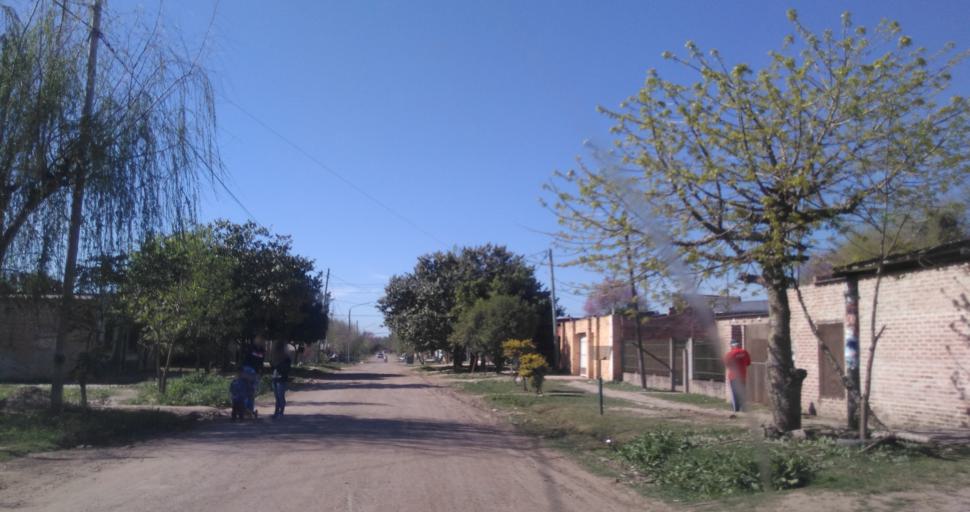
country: AR
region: Chaco
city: Fontana
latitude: -27.4228
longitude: -59.0281
